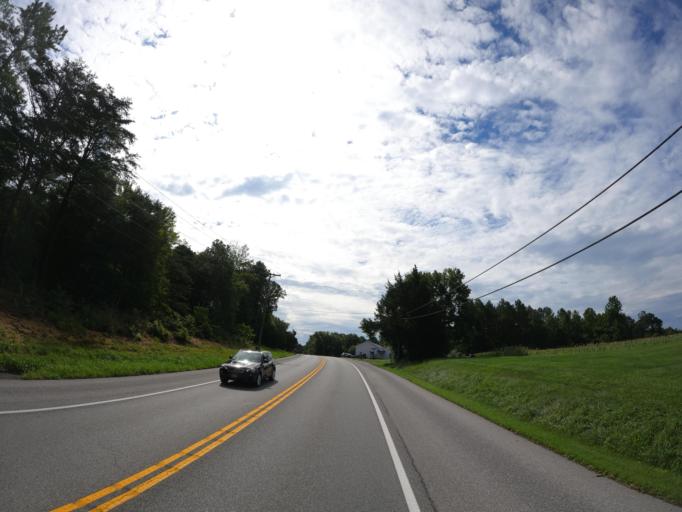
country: US
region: Maryland
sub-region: Saint Mary's County
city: Mechanicsville
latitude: 38.3729
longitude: -76.6926
